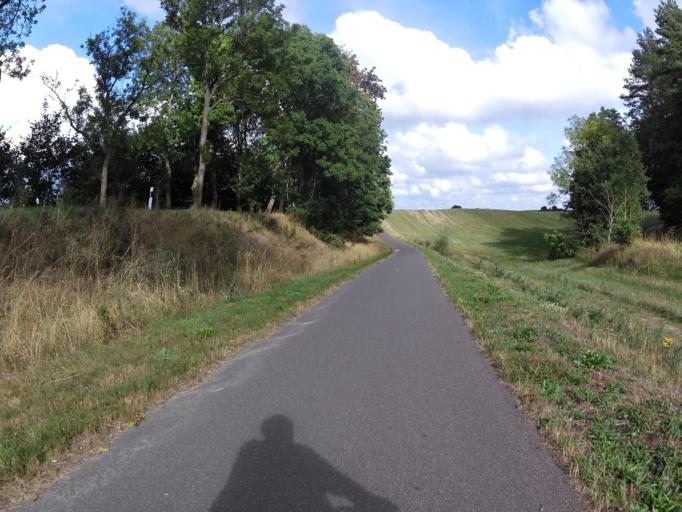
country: DE
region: Mecklenburg-Vorpommern
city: Seebad Bansin
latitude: 53.9414
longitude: 14.0829
